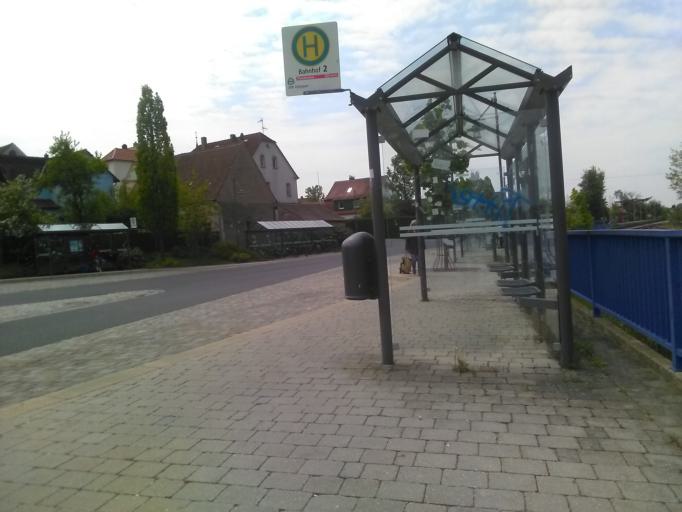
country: DE
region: Bavaria
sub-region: Upper Franconia
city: Kleinsendelbach
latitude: 49.5755
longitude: 11.2010
